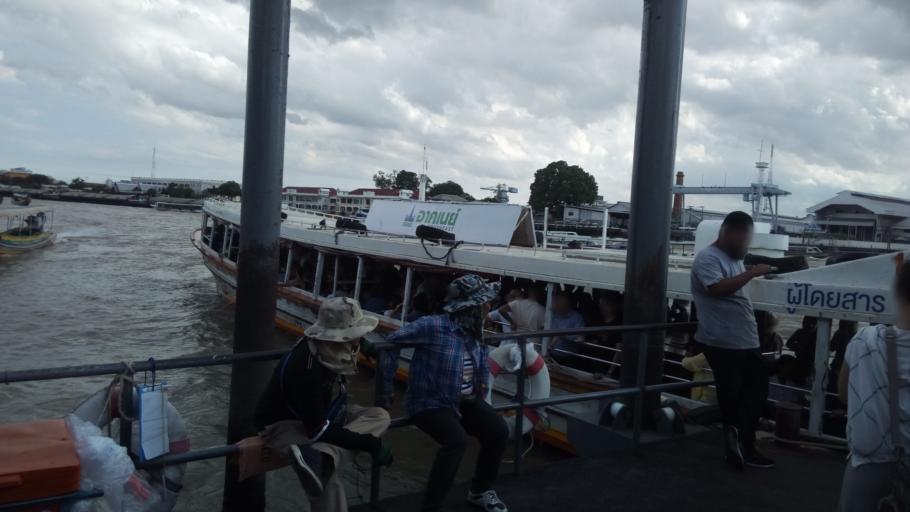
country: TH
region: Bangkok
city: Bangkok
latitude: 13.7523
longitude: 100.4882
